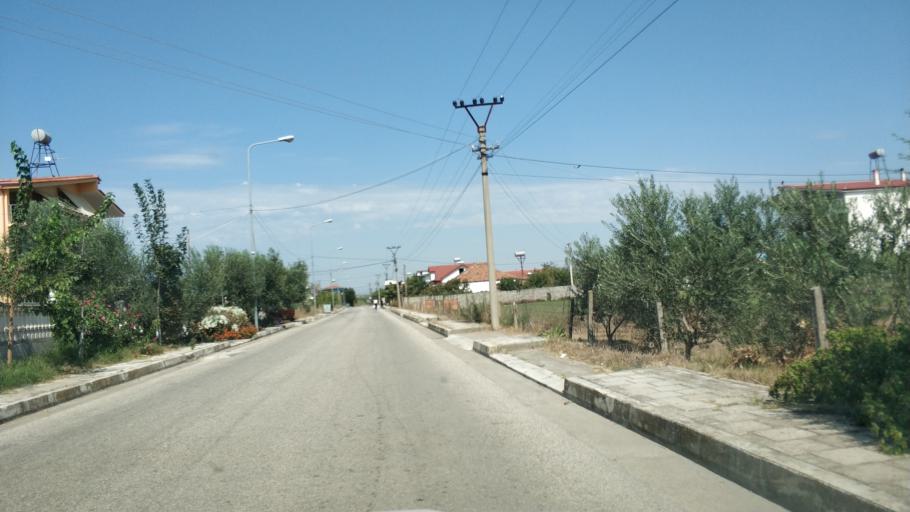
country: AL
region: Fier
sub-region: Rrethi i Lushnjes
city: Divjake
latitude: 41.0004
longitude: 19.5251
